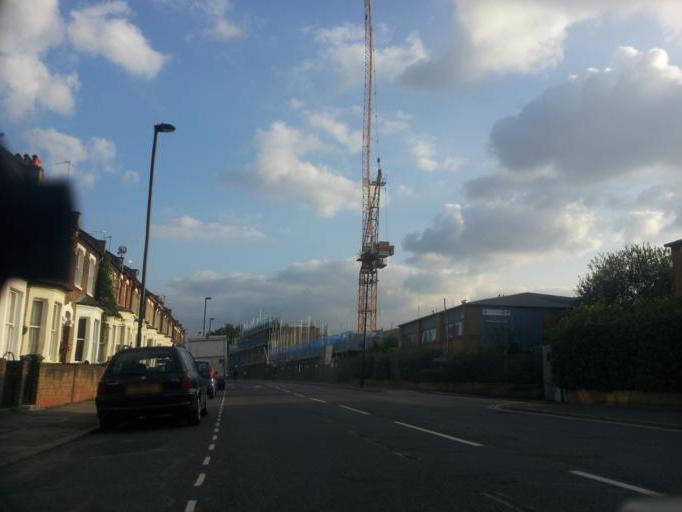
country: GB
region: England
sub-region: Greater London
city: Brixton
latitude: 51.4581
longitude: -0.1026
